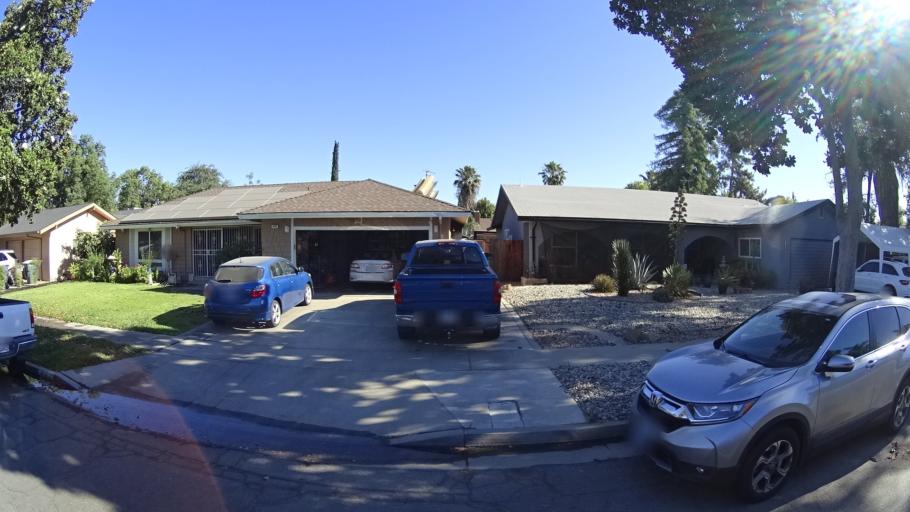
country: US
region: California
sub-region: Fresno County
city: Fresno
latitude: 36.7972
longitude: -119.8299
